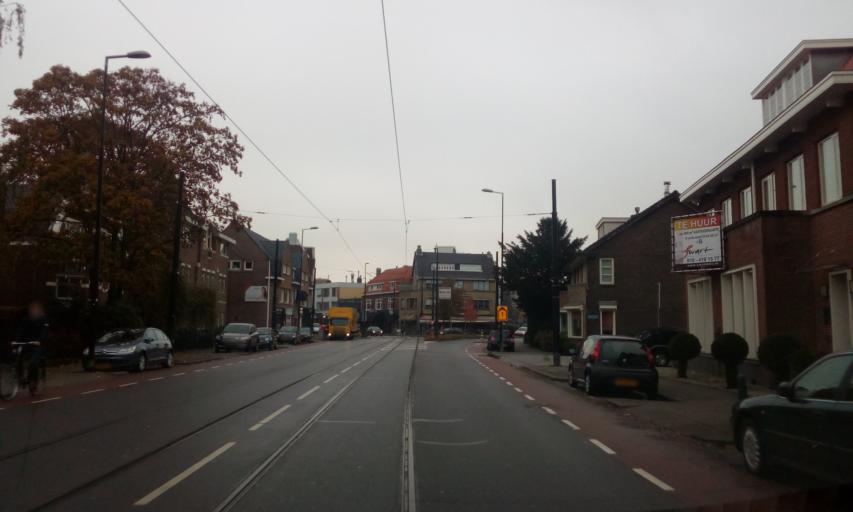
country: NL
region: South Holland
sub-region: Gemeente Rotterdam
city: Rotterdam
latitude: 51.9549
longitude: 4.4935
